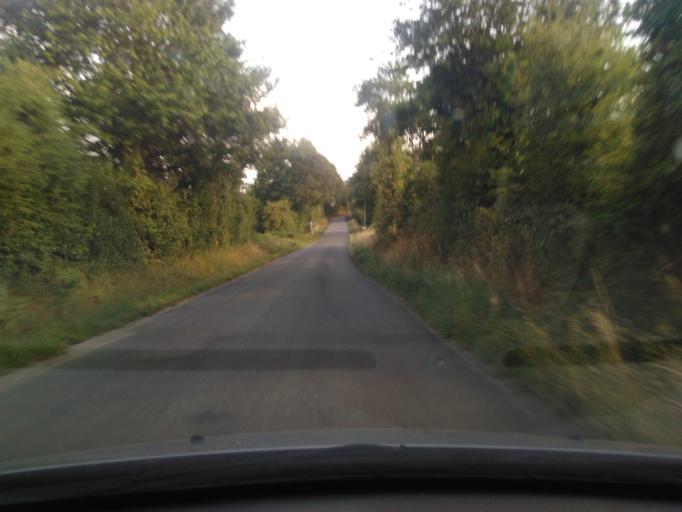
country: FR
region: Pays de la Loire
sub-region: Departement de la Vendee
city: Nesmy
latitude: 46.5941
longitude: -1.3626
